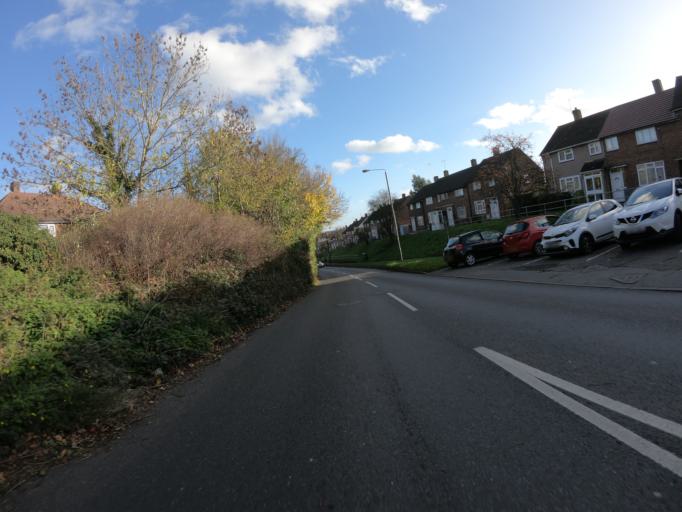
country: GB
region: England
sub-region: Greater London
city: Orpington
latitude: 51.3980
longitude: 0.1004
